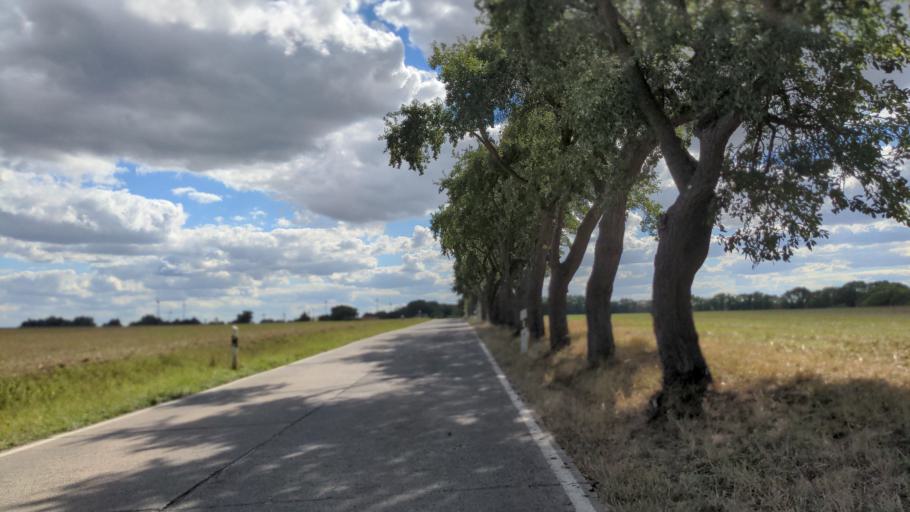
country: DE
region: Mecklenburg-Vorpommern
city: Gramkow
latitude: 53.9135
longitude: 11.3753
